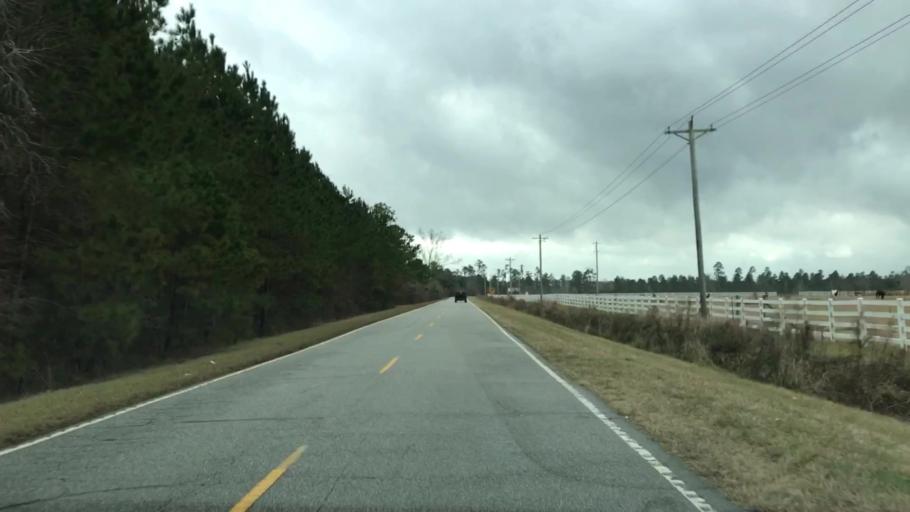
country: US
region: South Carolina
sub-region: Florence County
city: Johnsonville
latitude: 33.6538
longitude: -79.4193
